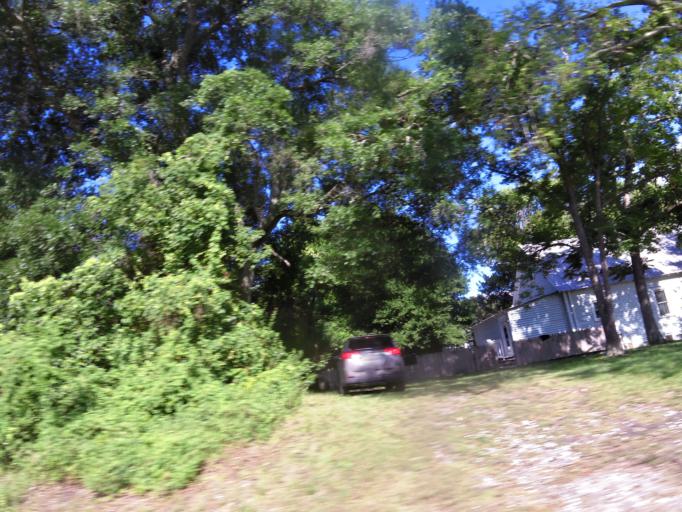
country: US
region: Florida
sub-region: Nassau County
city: Fernandina Beach
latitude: 30.6741
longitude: -81.4635
